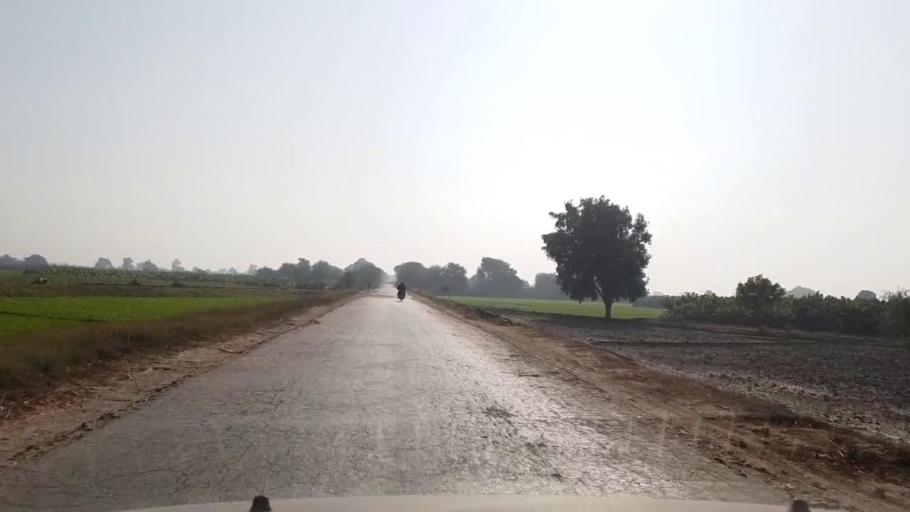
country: PK
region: Sindh
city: Matiari
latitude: 25.5492
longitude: 68.5445
